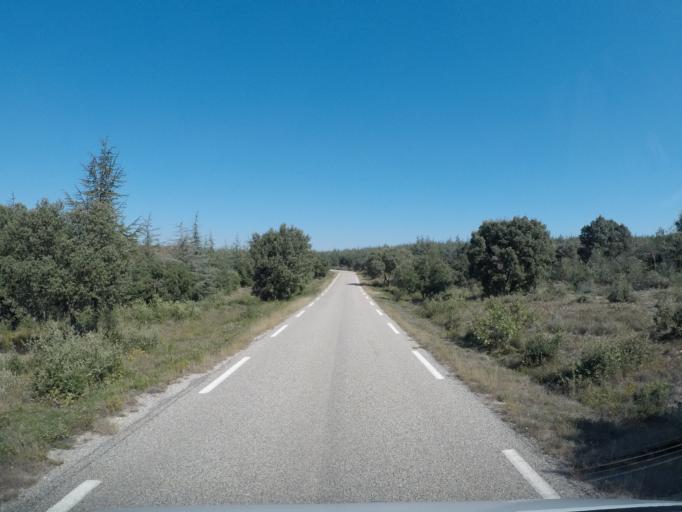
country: FR
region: Languedoc-Roussillon
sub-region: Departement du Gard
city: Saint-Victor-la-Coste
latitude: 44.0120
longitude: 4.6142
